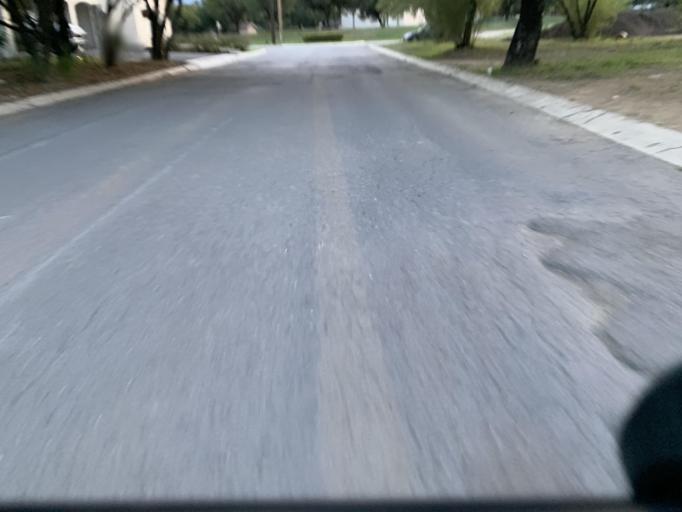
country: MX
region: Nuevo Leon
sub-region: Juarez
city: Bosques de San Pedro
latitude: 25.5183
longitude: -100.1967
